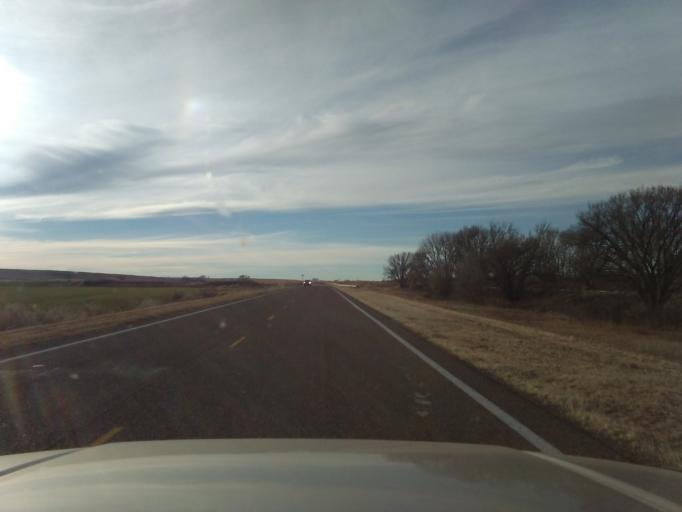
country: US
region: Kansas
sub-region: Norton County
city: Norton
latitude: 39.7567
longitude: -100.1155
